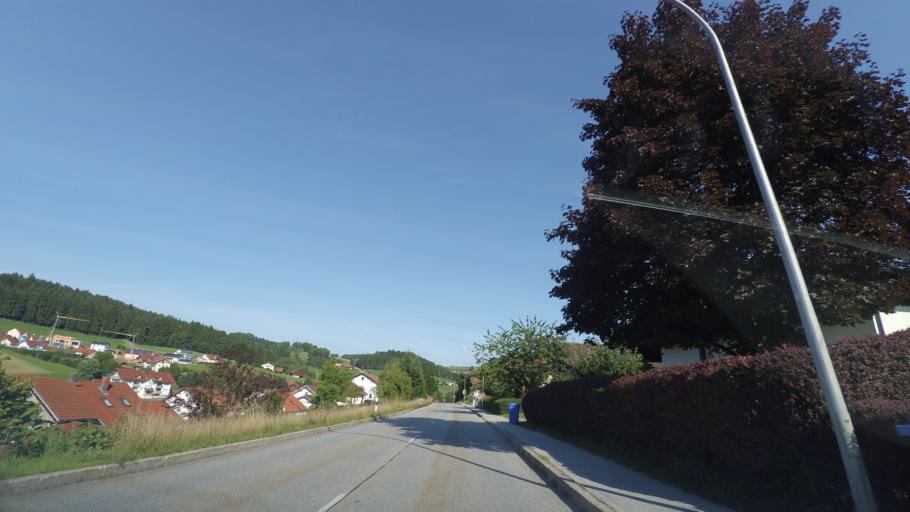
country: DE
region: Bavaria
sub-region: Lower Bavaria
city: Geiersthal
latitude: 49.0459
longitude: 12.9793
